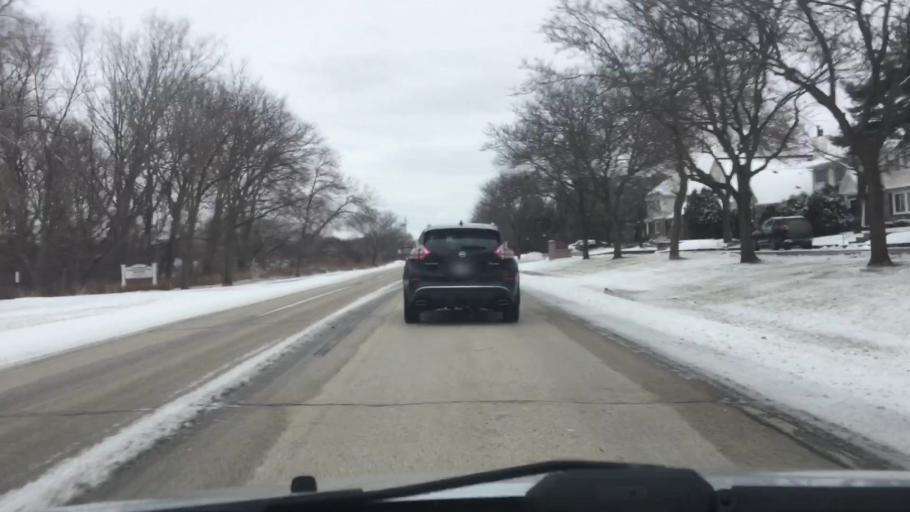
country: US
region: Wisconsin
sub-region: Waukesha County
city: Brookfield
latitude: 43.0437
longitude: -88.1061
